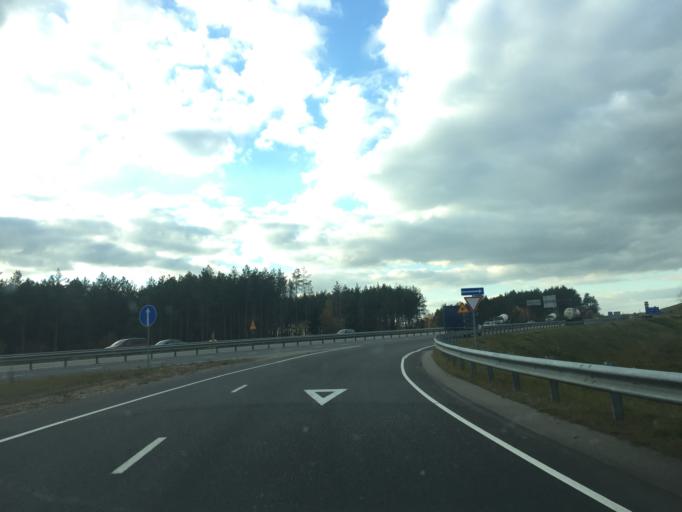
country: BY
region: Minsk
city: Rakaw
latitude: 53.9676
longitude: 27.0864
